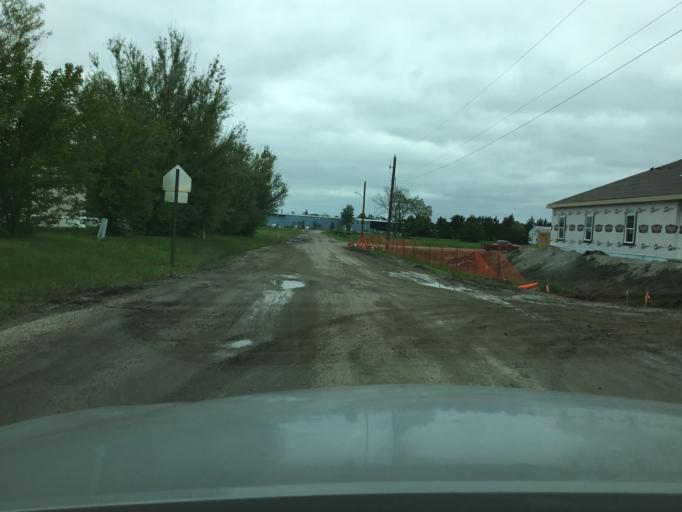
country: US
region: Kansas
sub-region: Franklin County
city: Ottawa
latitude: 38.6353
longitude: -95.2585
